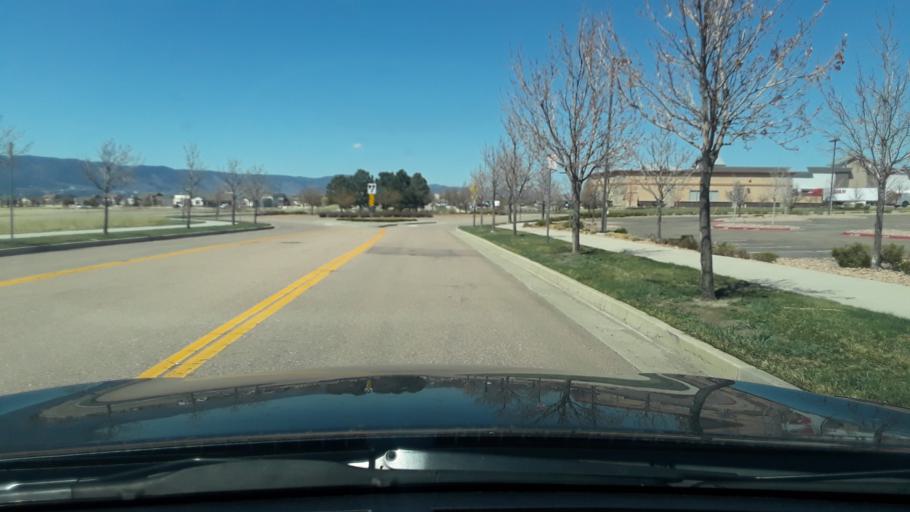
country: US
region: Colorado
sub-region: El Paso County
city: Black Forest
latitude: 38.9683
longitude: -104.7476
